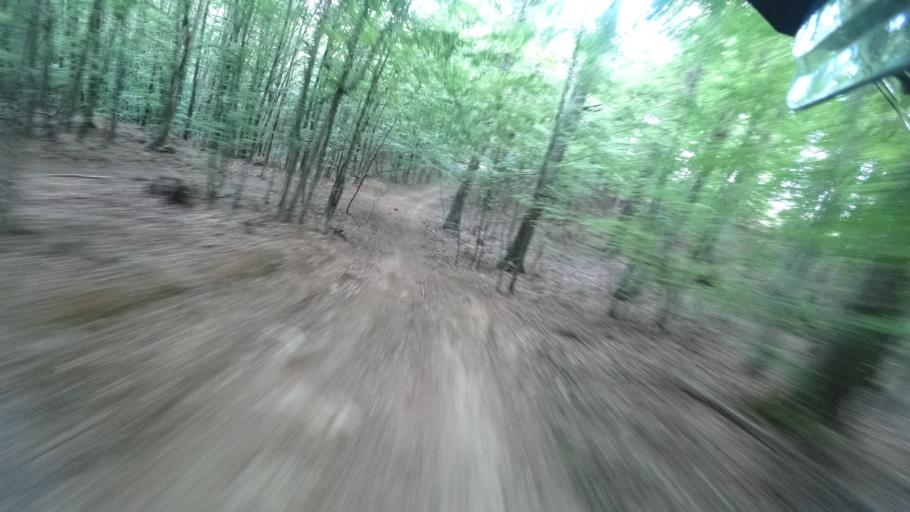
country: HR
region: Grad Zagreb
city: Stenjevec
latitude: 45.8488
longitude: 15.8940
